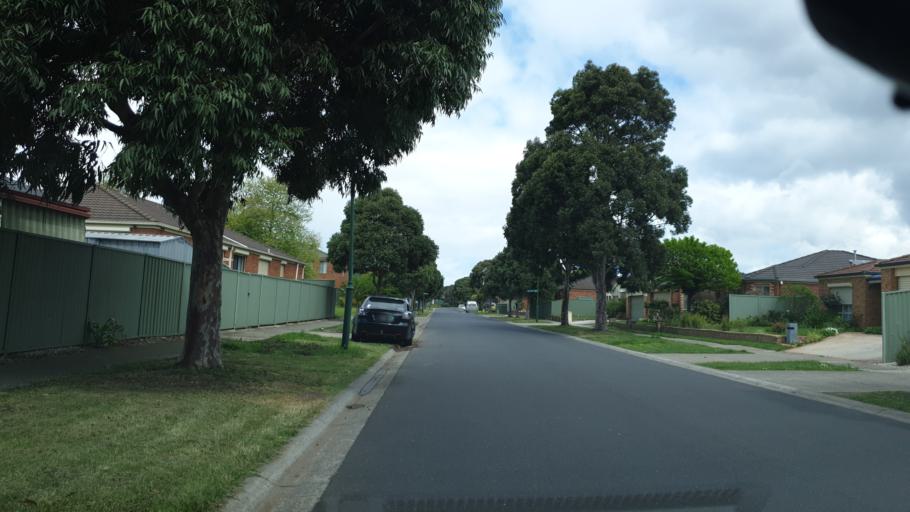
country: AU
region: Victoria
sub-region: Casey
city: Cranbourne
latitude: -38.1045
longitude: 145.2940
